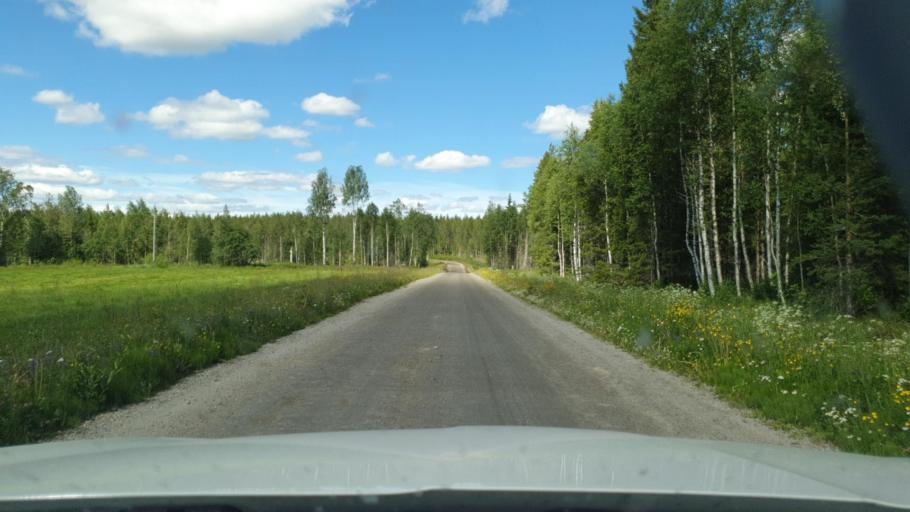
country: SE
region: Norrbotten
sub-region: Pitea Kommun
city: Roknas
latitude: 65.1581
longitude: 21.1575
